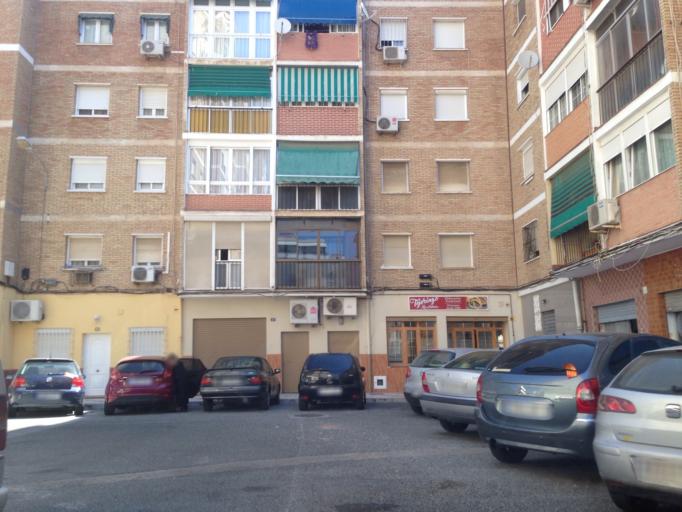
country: ES
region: Andalusia
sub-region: Provincia de Malaga
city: Malaga
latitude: 36.6976
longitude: -4.4443
